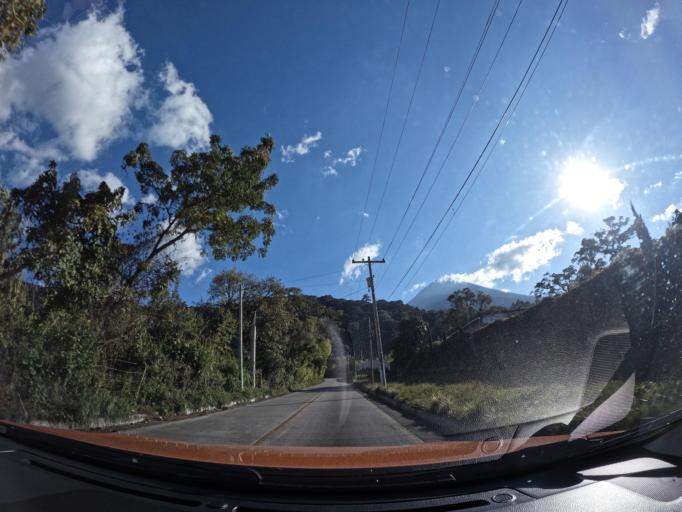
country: GT
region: Sacatepequez
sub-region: Municipio de Santa Maria de Jesus
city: Santa Maria de Jesus
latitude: 14.5153
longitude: -90.7222
